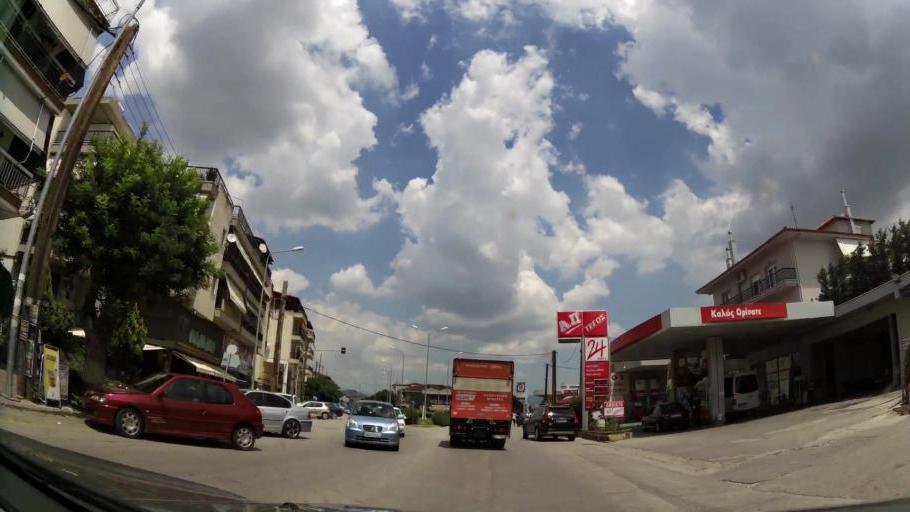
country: GR
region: West Macedonia
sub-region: Nomos Kozanis
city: Kozani
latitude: 40.2999
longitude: 21.7986
